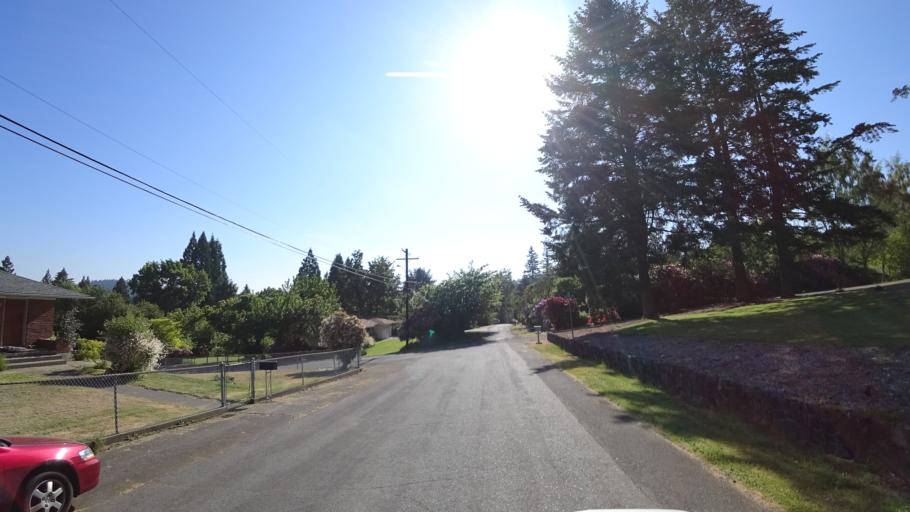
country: US
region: Oregon
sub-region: Clackamas County
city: Happy Valley
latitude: 45.4704
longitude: -122.5329
